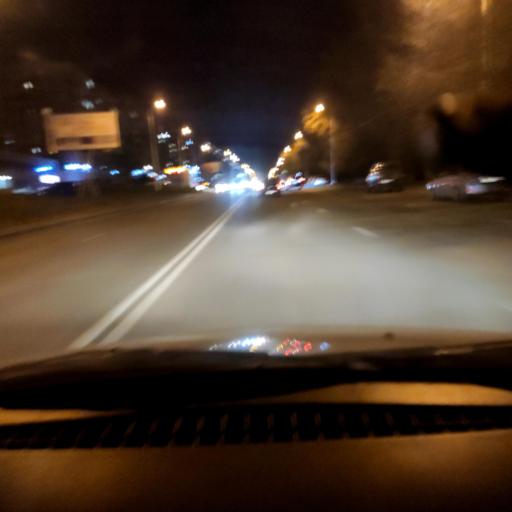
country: RU
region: Bashkortostan
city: Ufa
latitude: 54.7012
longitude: 55.9959
